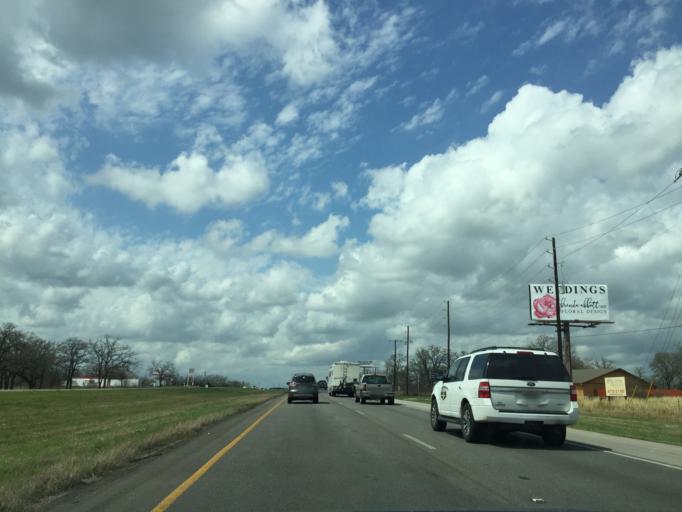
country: US
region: Texas
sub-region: Bastrop County
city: Wyldwood
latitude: 30.1268
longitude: -97.4405
